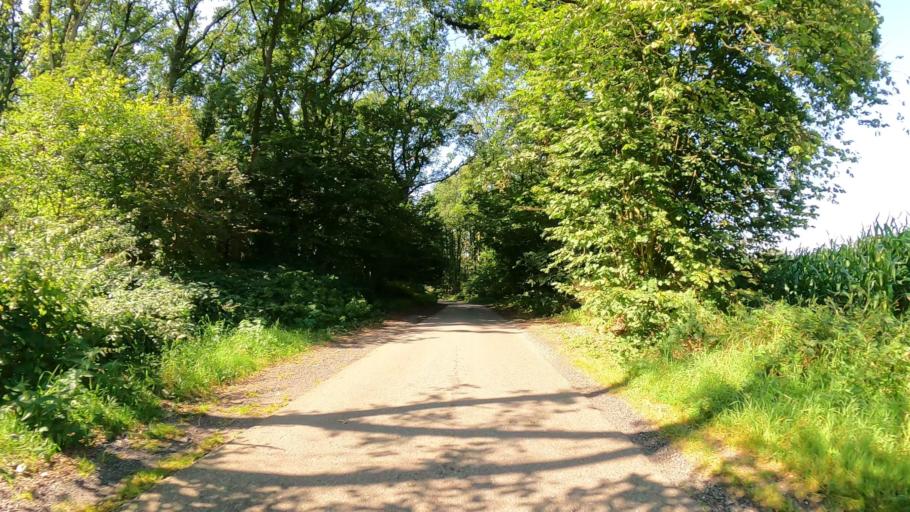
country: DE
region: Schleswig-Holstein
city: Nutzen
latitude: 53.8695
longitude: 9.9027
